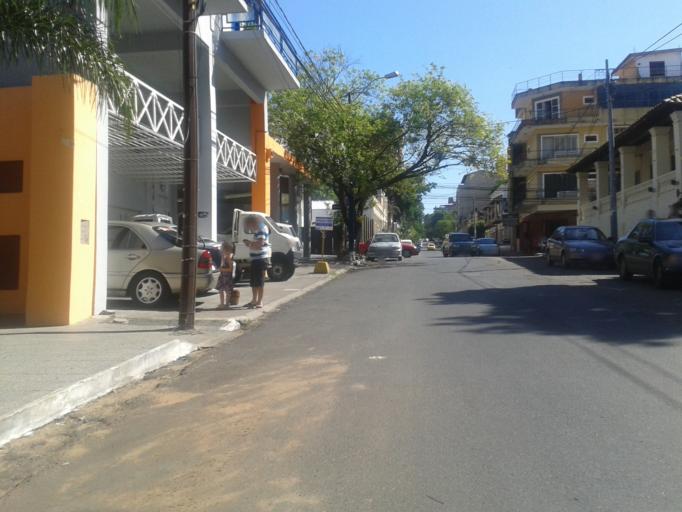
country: PY
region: Asuncion
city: Asuncion
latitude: -25.2865
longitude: -57.6406
